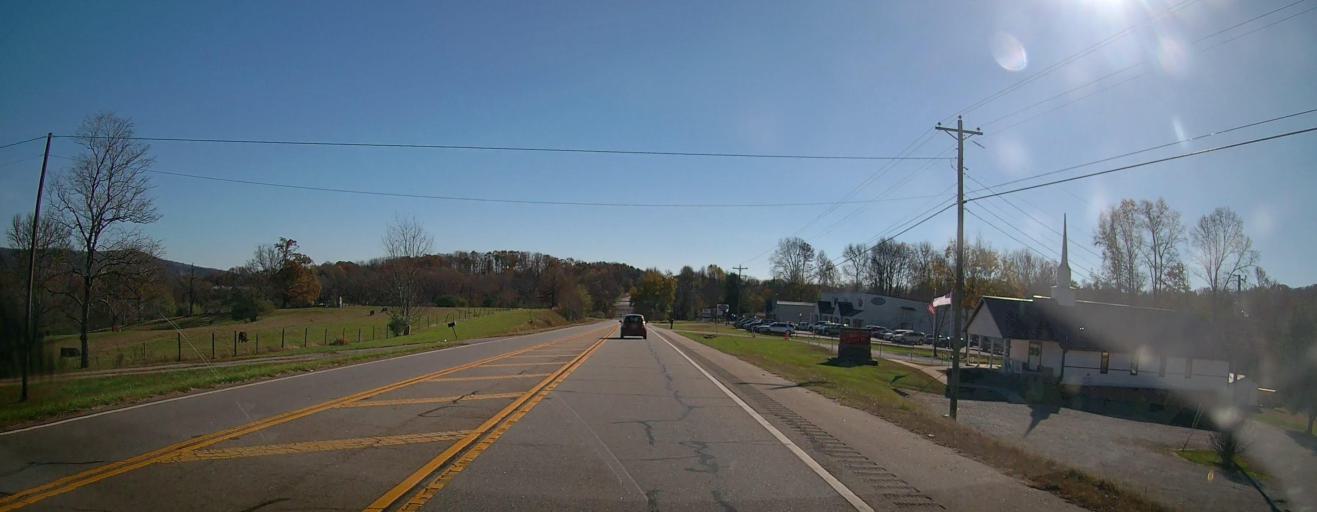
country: US
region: Georgia
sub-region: White County
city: Cleveland
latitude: 34.5209
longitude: -83.7551
